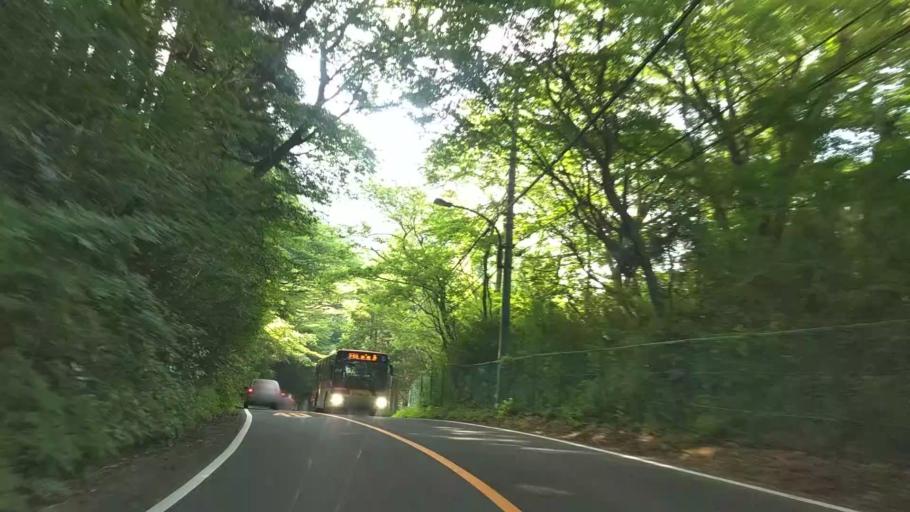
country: JP
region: Kanagawa
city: Hakone
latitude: 35.2277
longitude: 139.0494
